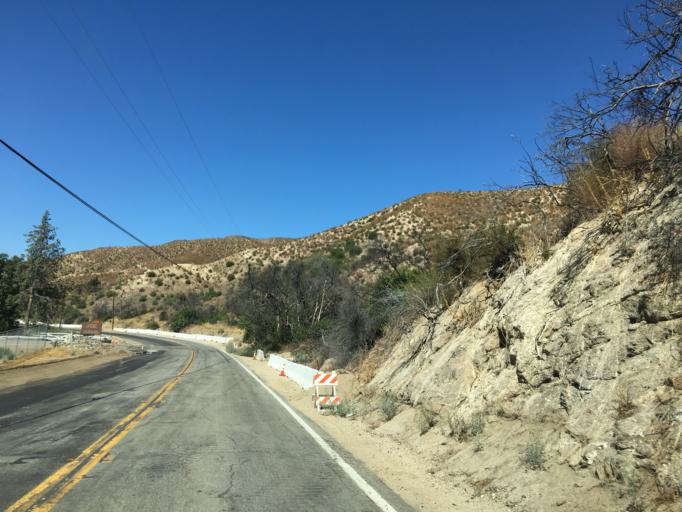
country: US
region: California
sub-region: Los Angeles County
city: Green Valley
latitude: 34.6541
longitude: -118.4783
